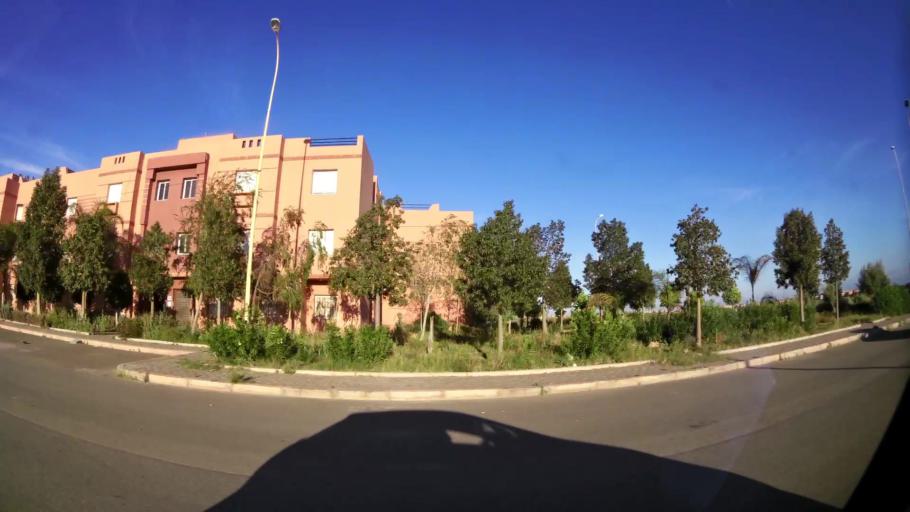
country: MA
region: Marrakech-Tensift-Al Haouz
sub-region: Marrakech
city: Marrakesh
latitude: 31.7500
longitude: -8.1290
